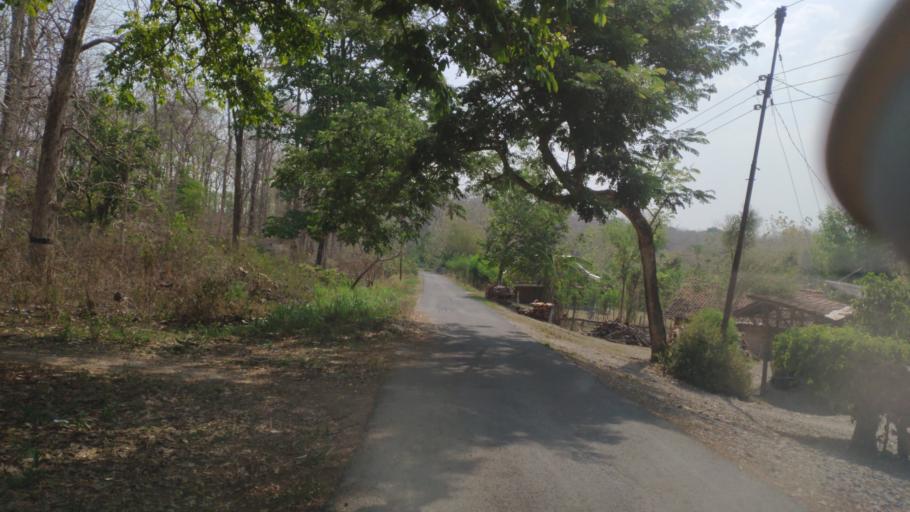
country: ID
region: Central Java
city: Randublatung
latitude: -7.2320
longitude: 111.2912
